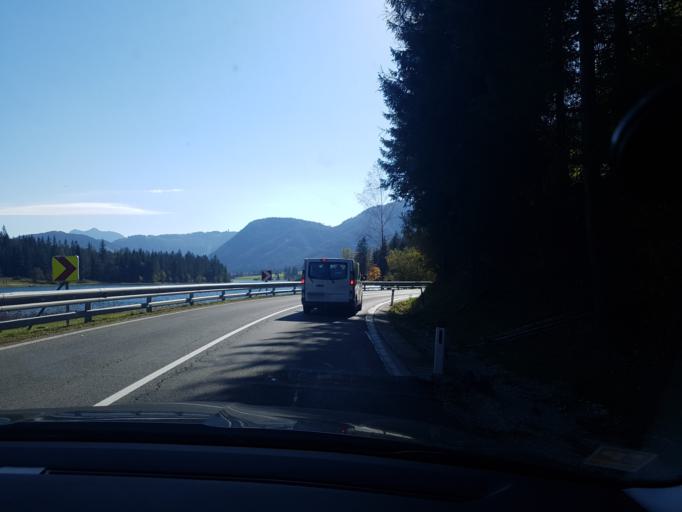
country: AT
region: Tyrol
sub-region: Politischer Bezirk Kitzbuhel
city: Waidring
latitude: 47.5457
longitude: 12.5679
